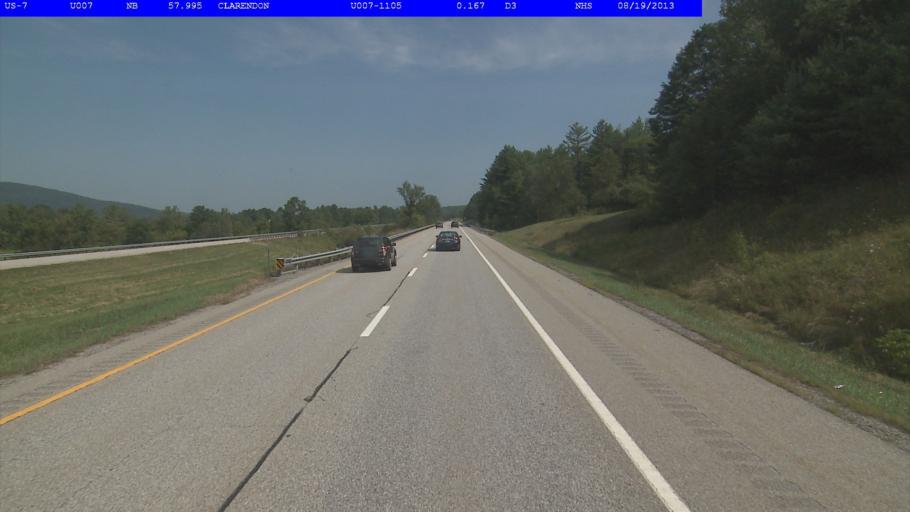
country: US
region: Vermont
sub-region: Rutland County
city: Rutland
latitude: 43.4964
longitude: -72.9687
